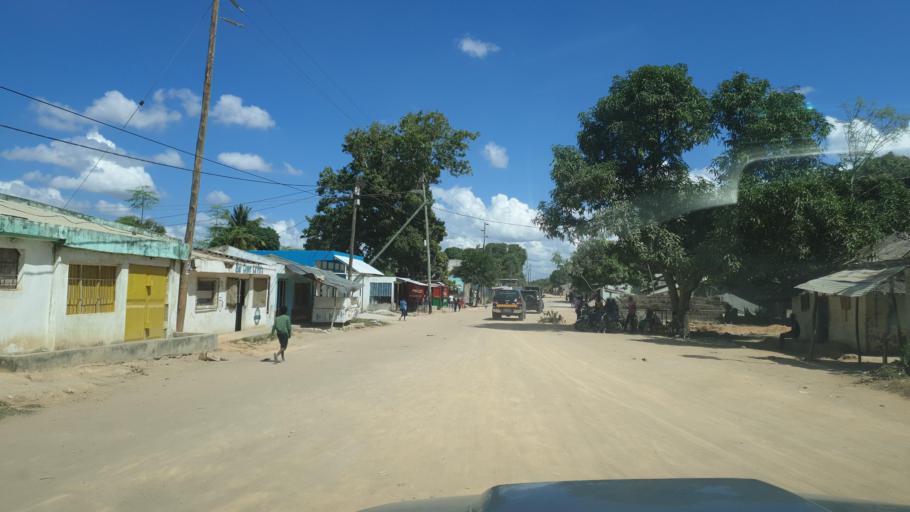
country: MZ
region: Nampula
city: Nacala
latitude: -14.5721
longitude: 40.6927
